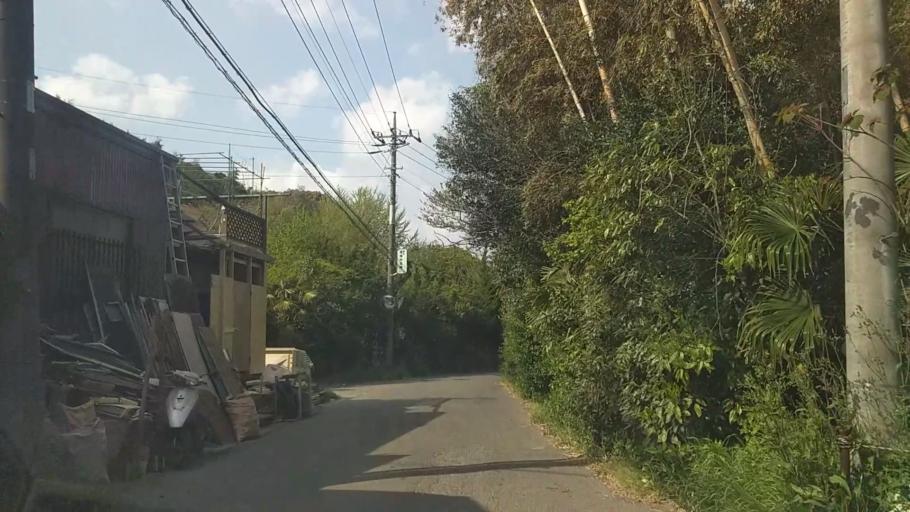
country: JP
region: Kanagawa
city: Kamakura
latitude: 35.3825
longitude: 139.5646
